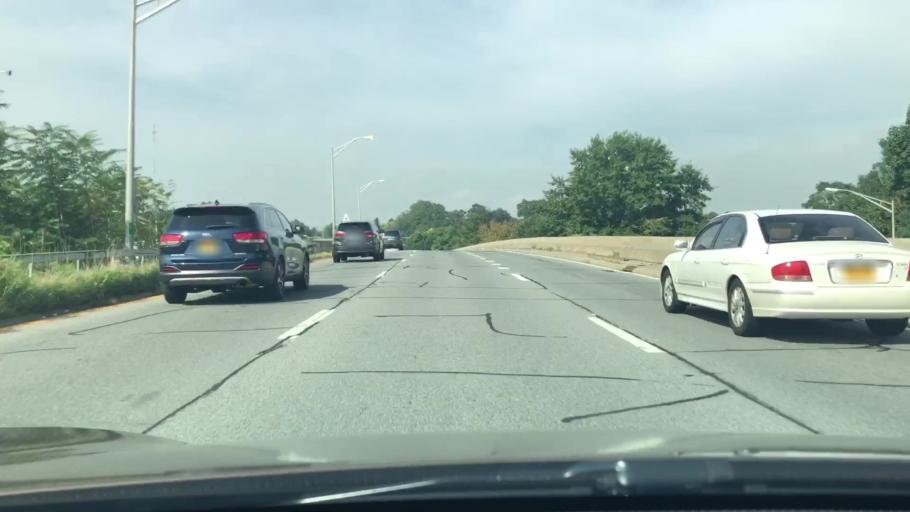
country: US
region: New York
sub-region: Westchester County
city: Bronxville
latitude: 40.9312
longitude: -73.8543
